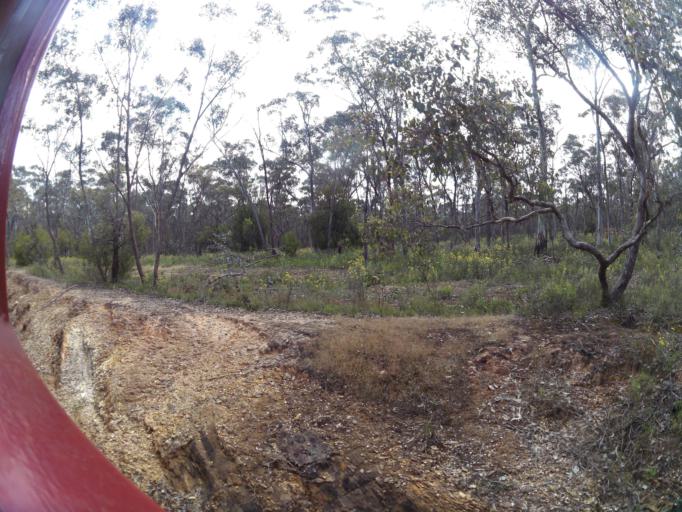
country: AU
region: Victoria
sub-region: Mount Alexander
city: Castlemaine
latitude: -37.0507
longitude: 144.1852
